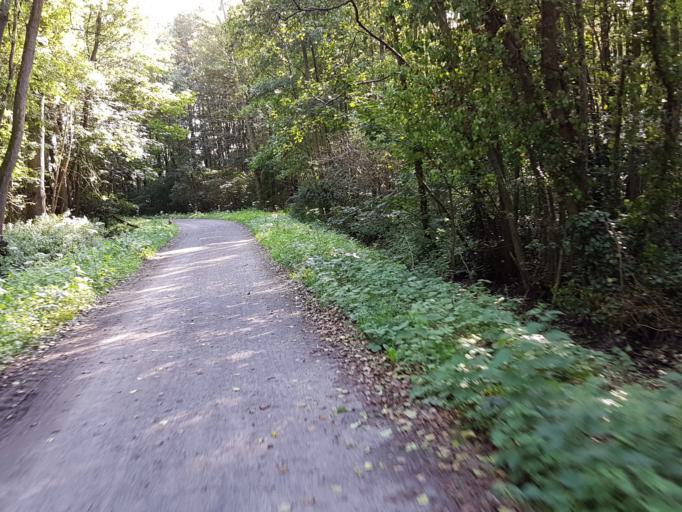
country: BE
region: Flanders
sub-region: Provincie Vlaams-Brabant
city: Steenokkerzeel
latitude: 50.9217
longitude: 4.4810
